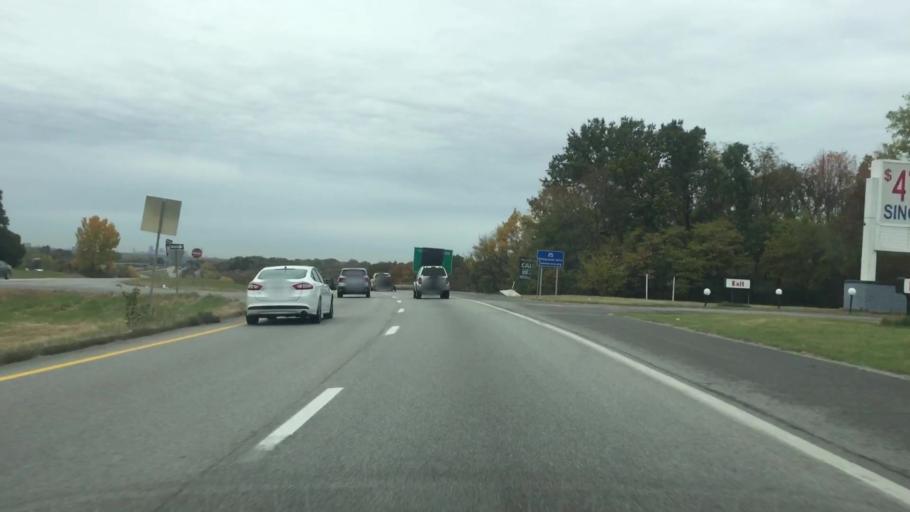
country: US
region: Missouri
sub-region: Jackson County
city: Raytown
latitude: 39.0058
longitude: -94.4853
